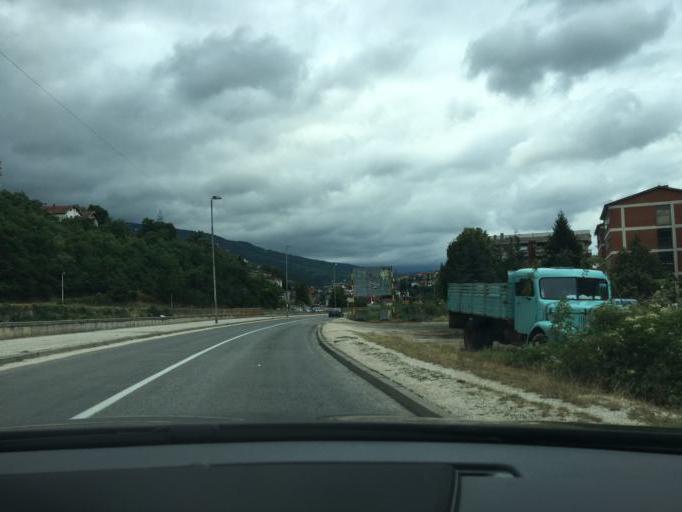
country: MK
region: Kriva Palanka
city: Kriva Palanka
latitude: 42.2096
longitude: 22.3403
